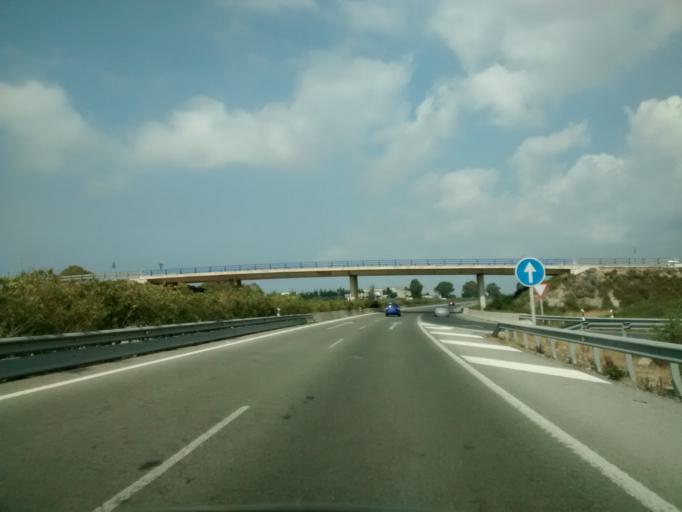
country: ES
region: Andalusia
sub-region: Provincia de Cadiz
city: Chiclana de la Frontera
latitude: 36.3558
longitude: -6.1027
